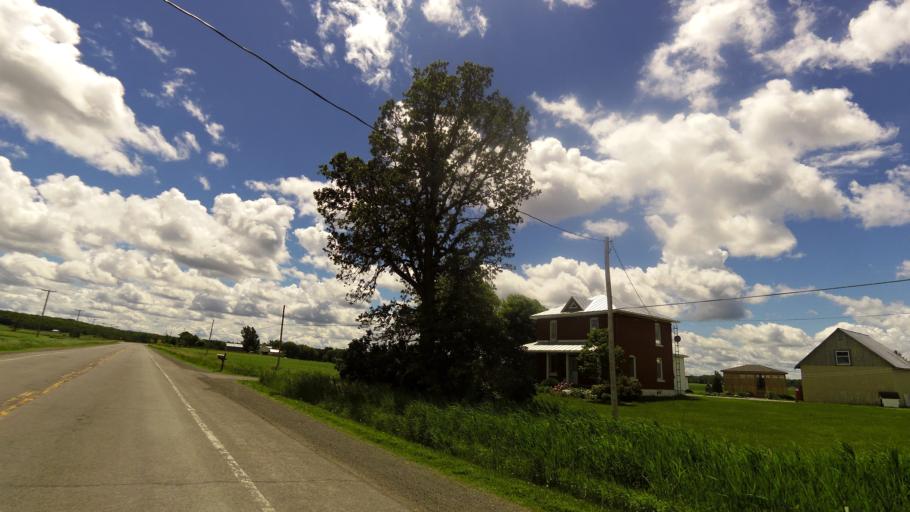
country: CA
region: Quebec
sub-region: Monteregie
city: Hudson
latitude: 45.5150
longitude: -74.1619
